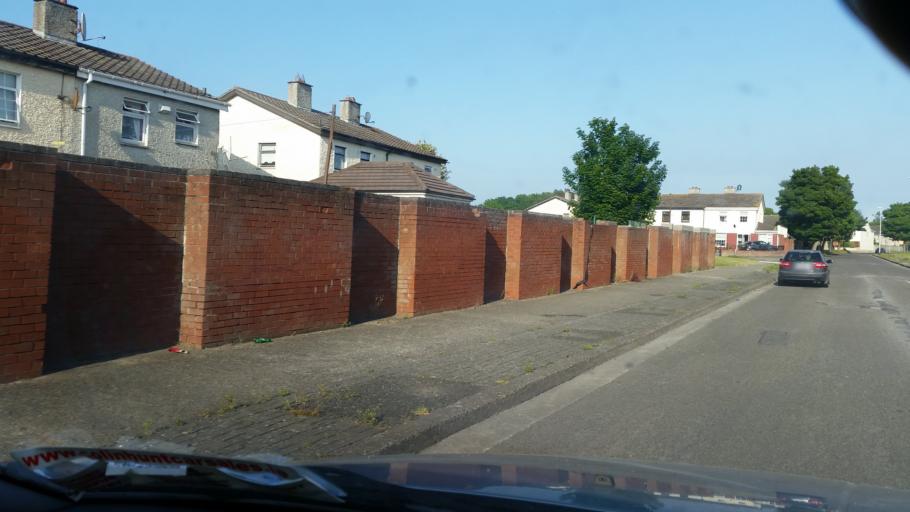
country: IE
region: Leinster
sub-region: Fingal County
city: Blanchardstown
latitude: 53.4013
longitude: -6.3735
